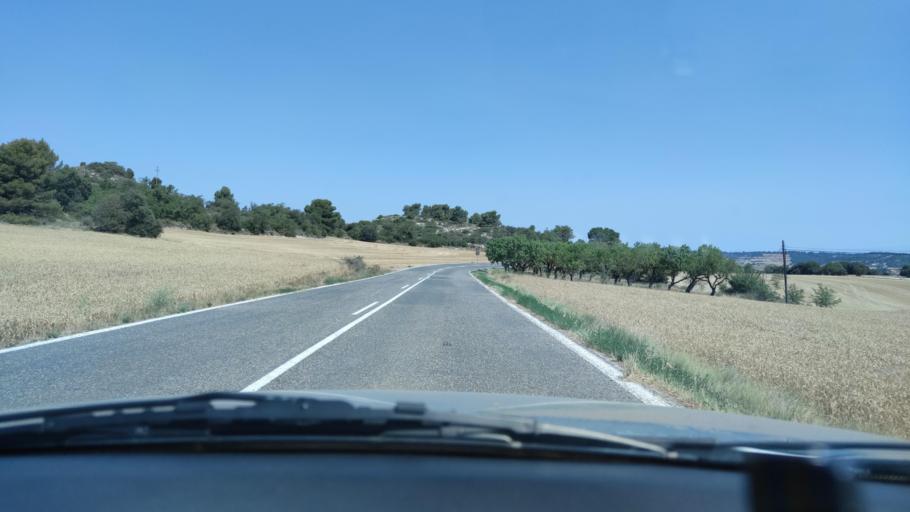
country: ES
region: Catalonia
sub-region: Provincia de Tarragona
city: Santa Coloma de Queralt
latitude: 41.6085
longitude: 1.3449
